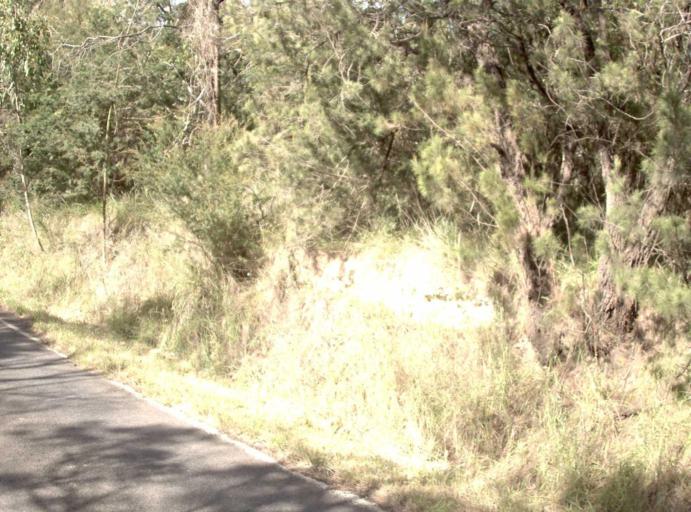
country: AU
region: Victoria
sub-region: Latrobe
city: Morwell
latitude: -38.1911
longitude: 146.4038
